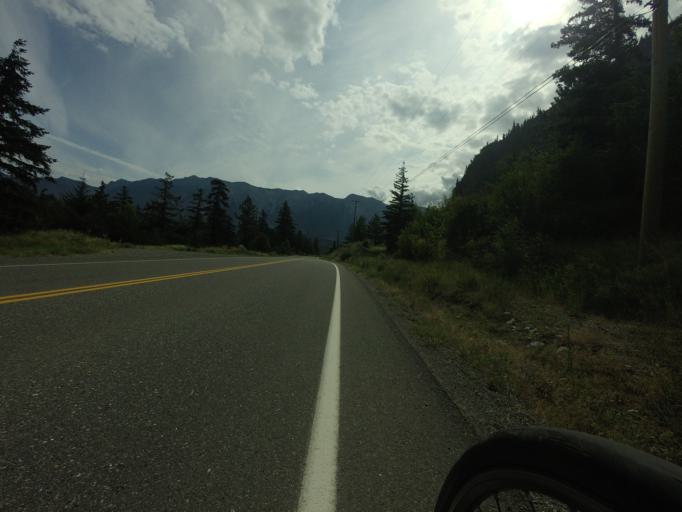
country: CA
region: British Columbia
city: Lillooet
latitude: 50.6703
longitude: -121.9552
